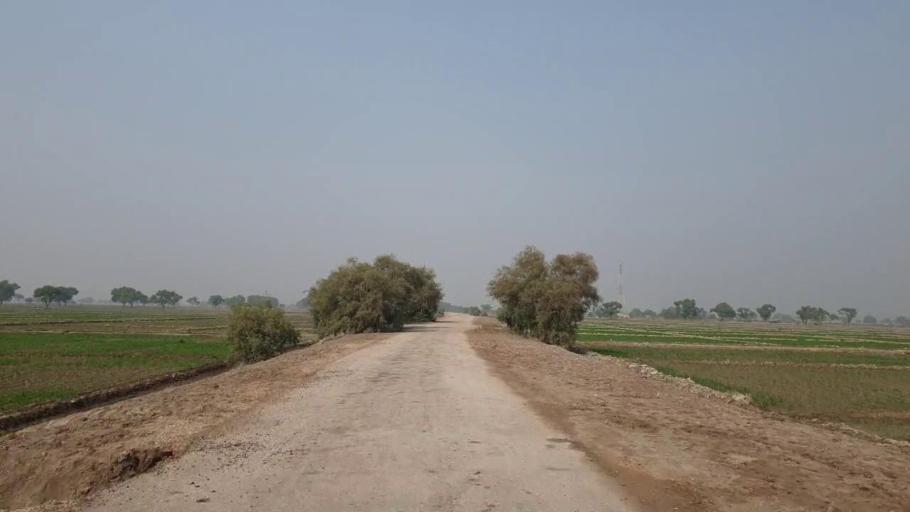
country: PK
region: Sindh
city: Bhan
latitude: 26.4934
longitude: 67.6994
